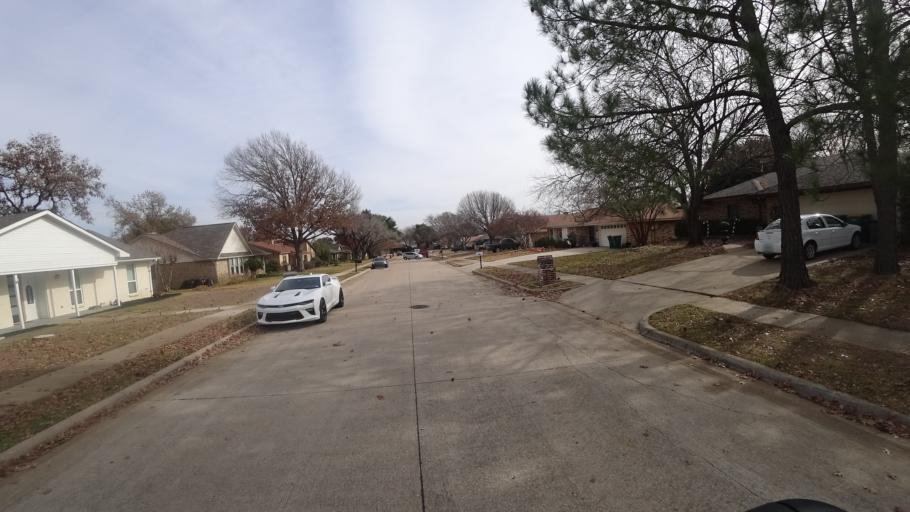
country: US
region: Texas
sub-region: Denton County
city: Highland Village
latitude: 33.0769
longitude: -97.0295
